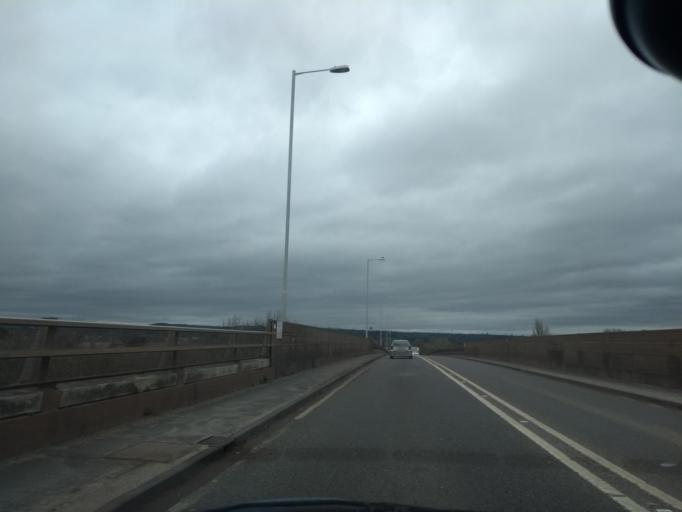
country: GB
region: England
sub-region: Somerset
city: Taunton
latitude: 51.0237
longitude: -3.0901
